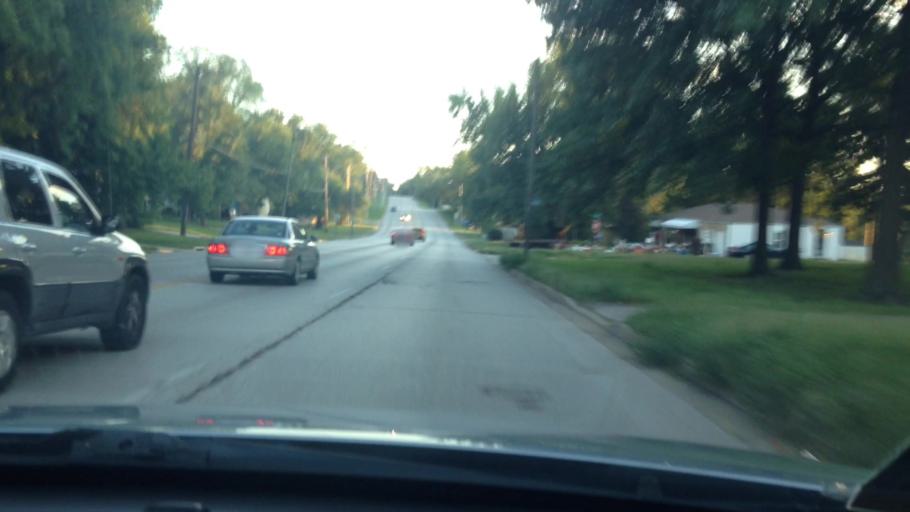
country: US
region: Missouri
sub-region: Jackson County
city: Raytown
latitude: 38.9897
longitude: -94.4828
